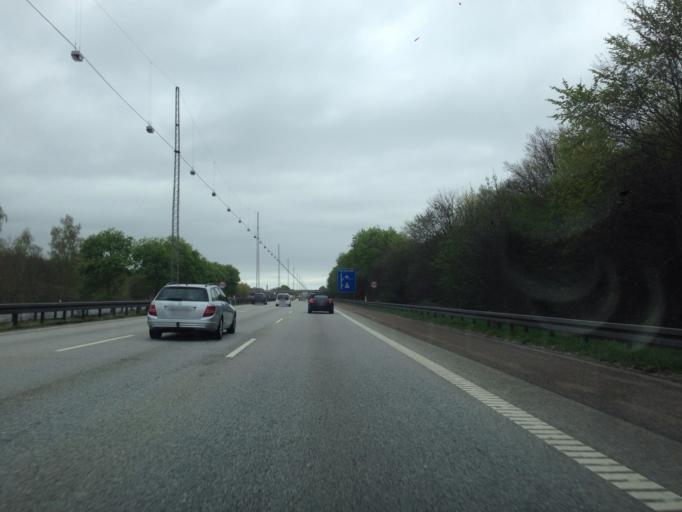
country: DK
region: Capital Region
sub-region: Lyngby-Tarbaek Kommune
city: Kongens Lyngby
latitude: 55.7831
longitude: 12.5274
